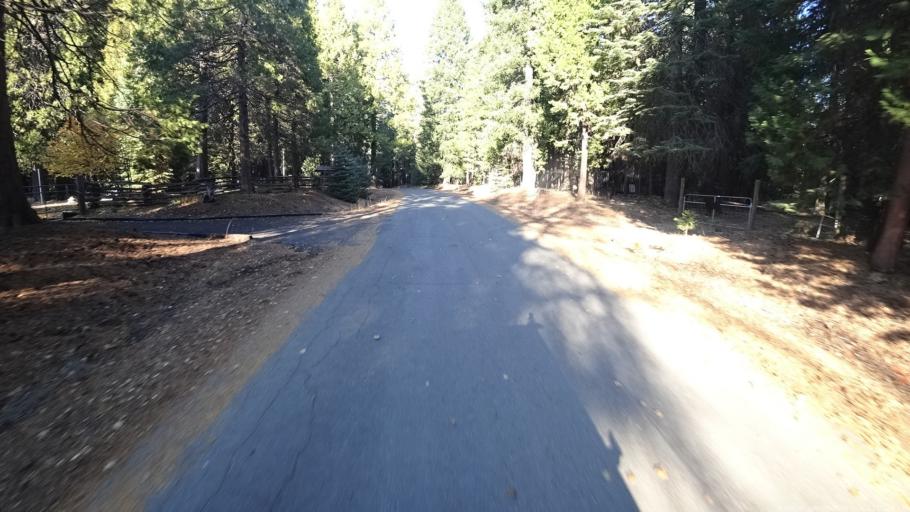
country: US
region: California
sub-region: Shasta County
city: Shingletown
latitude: 40.5525
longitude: -121.7224
